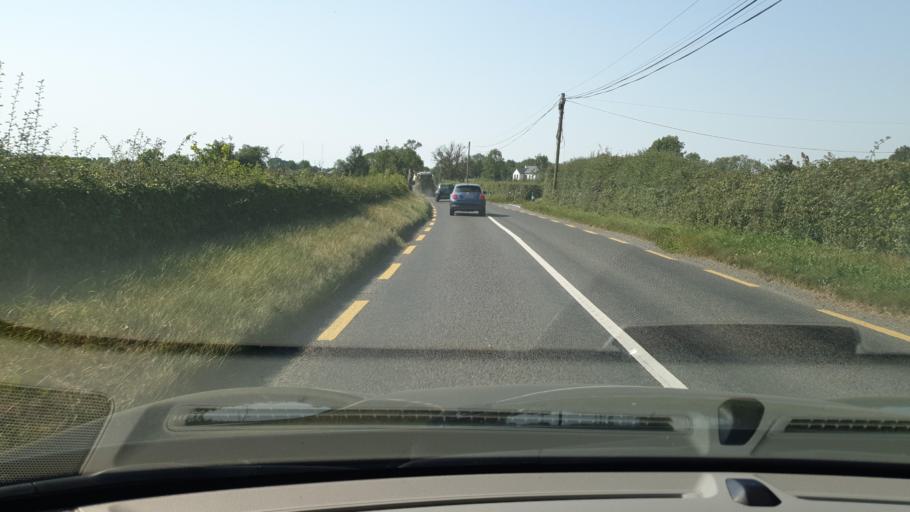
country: IE
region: Leinster
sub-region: An Mhi
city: Trim
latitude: 53.5785
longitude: -6.8382
